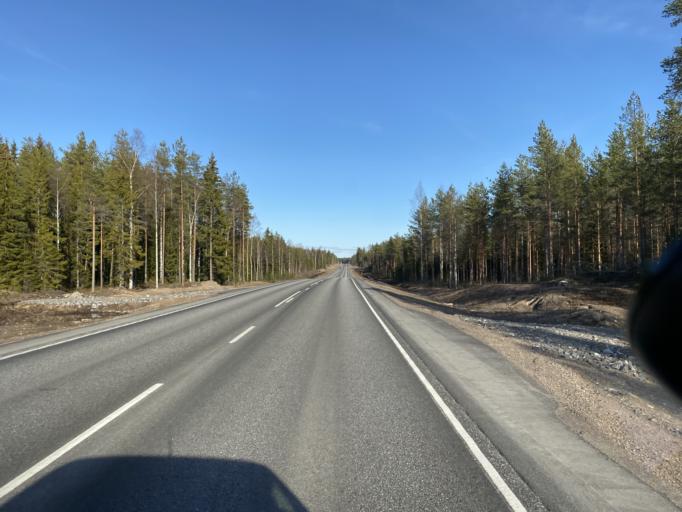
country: FI
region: Satakunta
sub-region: Pori
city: Kokemaeki
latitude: 61.1664
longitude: 22.4020
